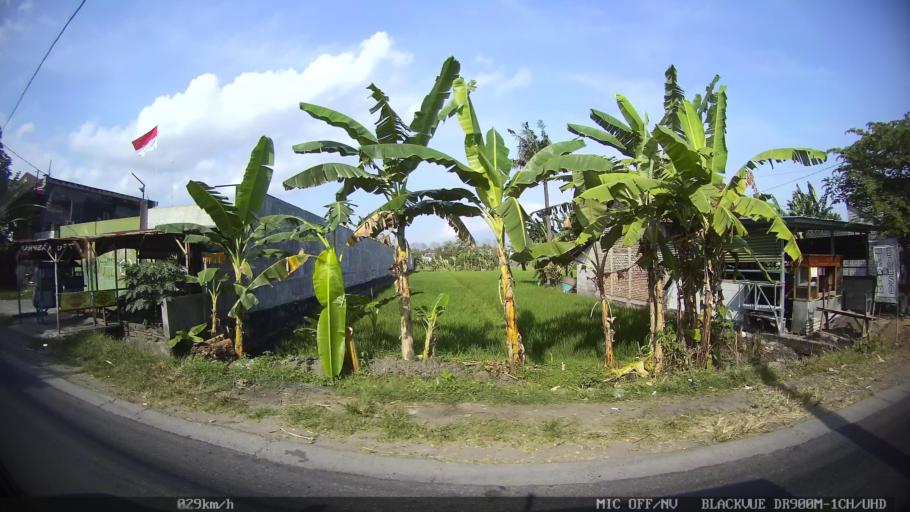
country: ID
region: Daerah Istimewa Yogyakarta
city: Kasihan
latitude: -7.8411
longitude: 110.3440
